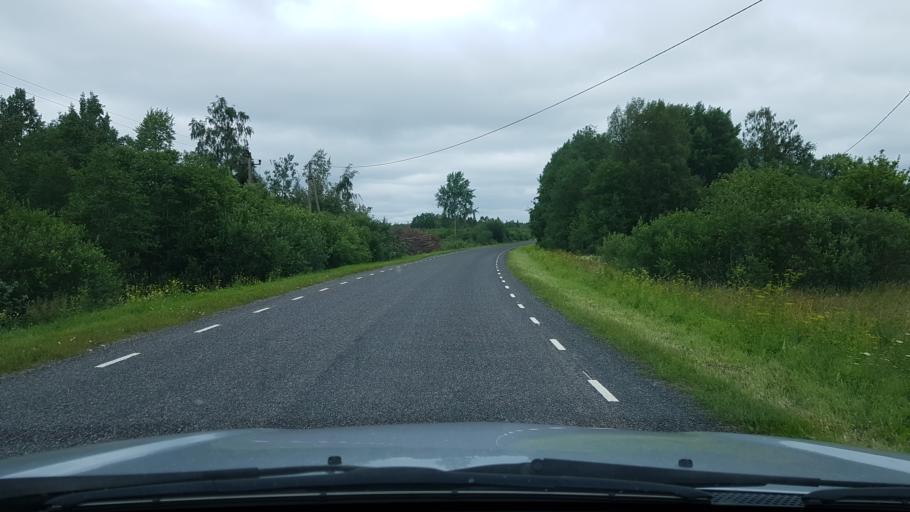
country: EE
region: Ida-Virumaa
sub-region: Narva-Joesuu linn
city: Narva-Joesuu
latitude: 59.3748
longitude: 28.0697
